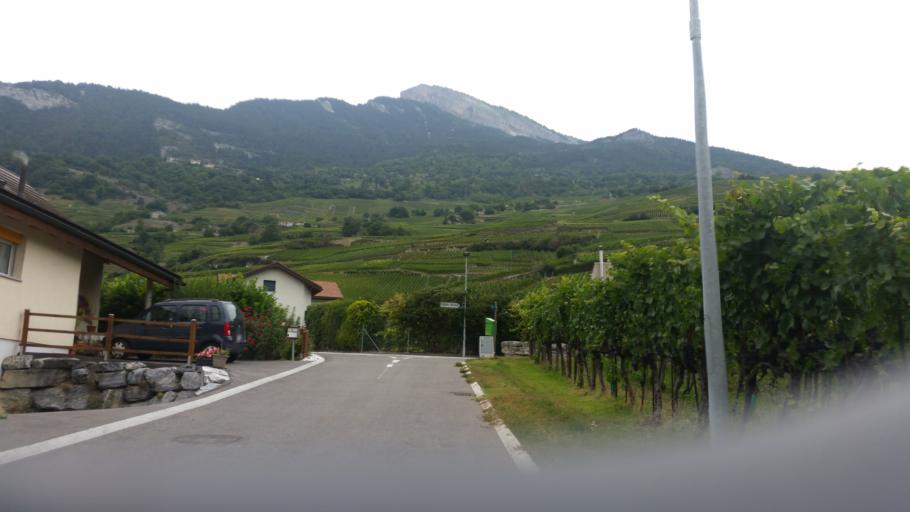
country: CH
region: Valais
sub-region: Conthey District
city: Vetroz
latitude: 46.2266
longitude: 7.2870
